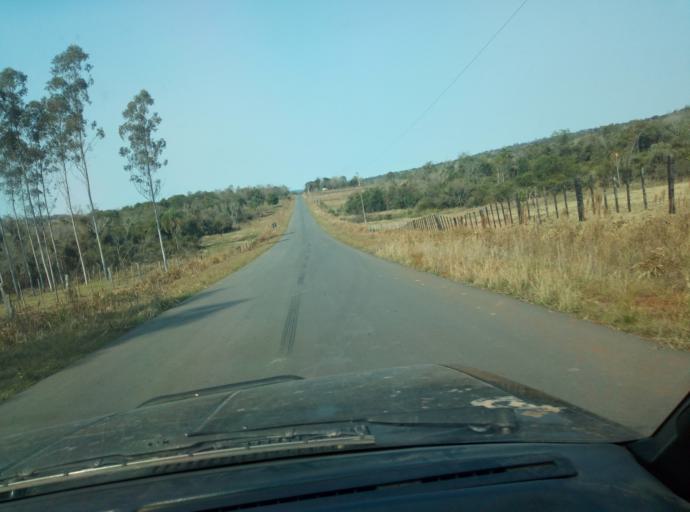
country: PY
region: Caaguazu
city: Carayao
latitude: -25.2571
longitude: -56.2879
